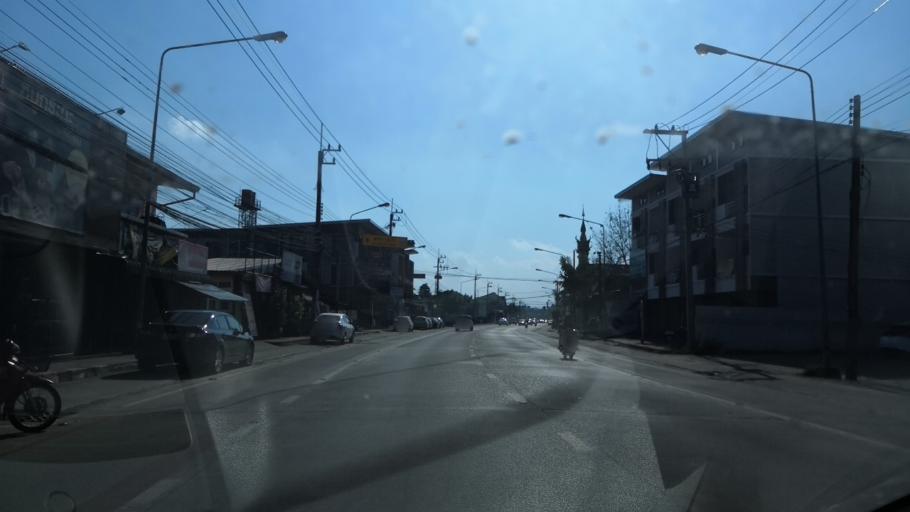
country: TH
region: Chiang Rai
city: Chiang Rai
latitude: 19.9287
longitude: 99.8386
